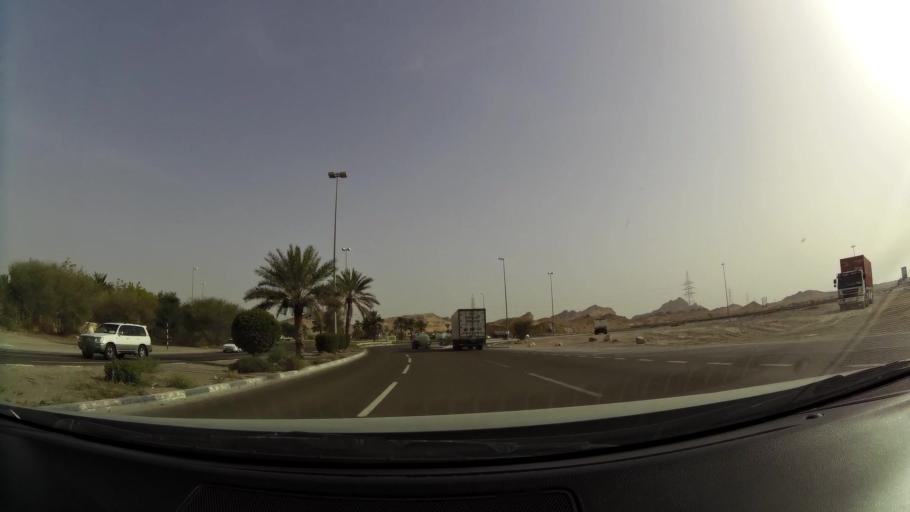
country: AE
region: Abu Dhabi
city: Al Ain
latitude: 24.1386
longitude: 55.7379
